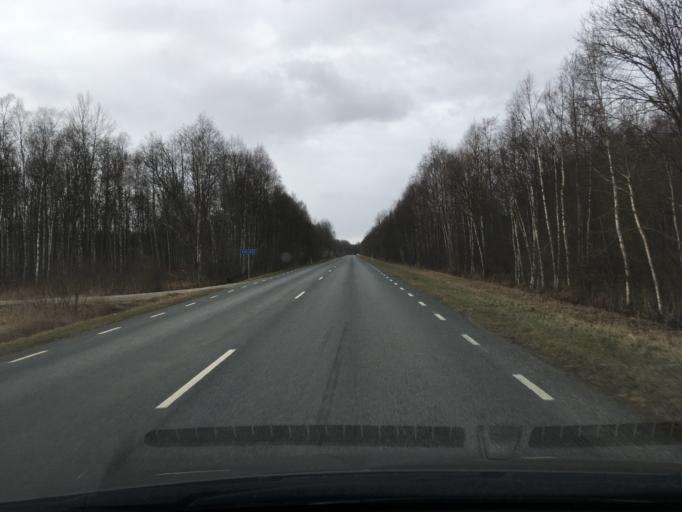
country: EE
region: Laeaene
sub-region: Lihula vald
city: Lihula
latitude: 58.6440
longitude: 23.8505
